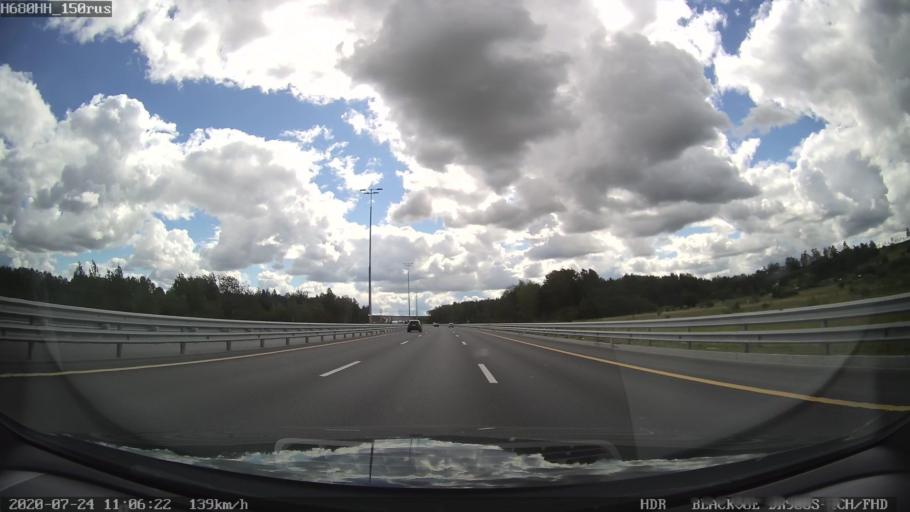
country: RU
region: St.-Petersburg
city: Shushary
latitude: 59.7641
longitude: 30.3736
